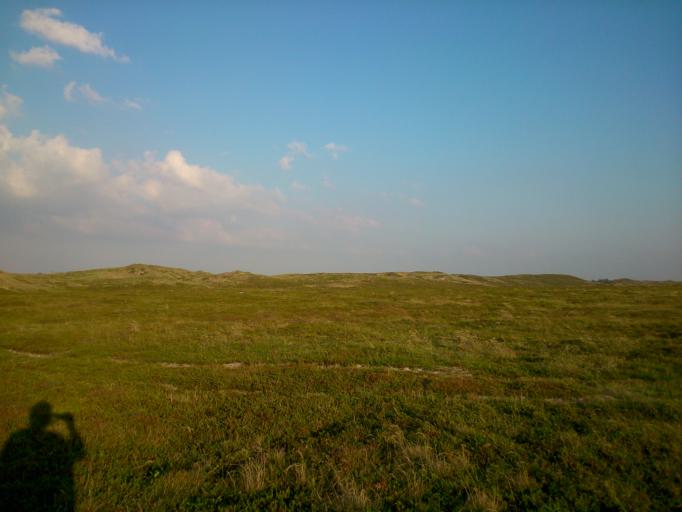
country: DK
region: Central Jutland
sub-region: Ringkobing-Skjern Kommune
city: Hvide Sande
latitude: 55.8798
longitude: 8.1591
